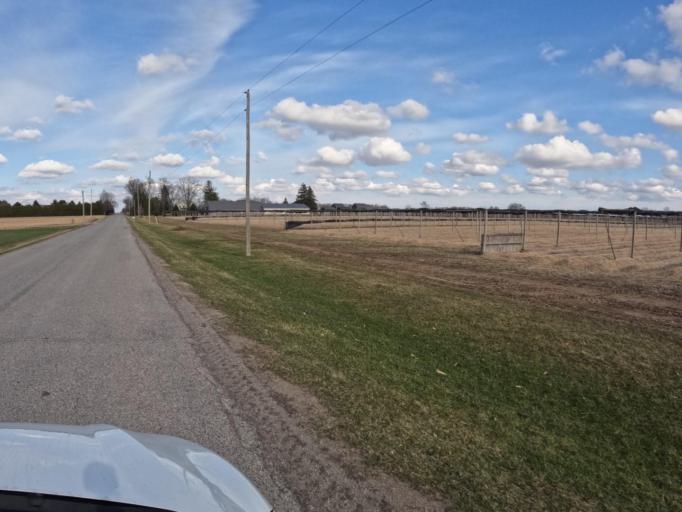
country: CA
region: Ontario
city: Brant
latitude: 42.9945
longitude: -80.3983
